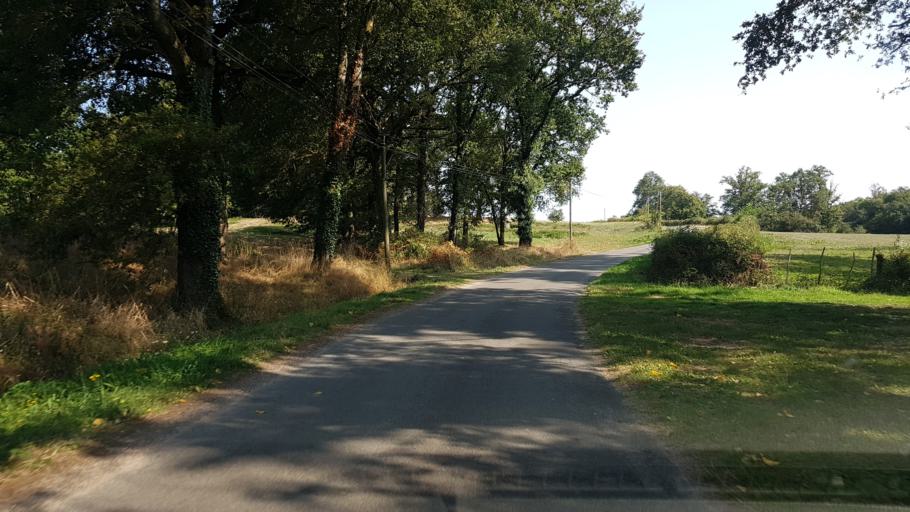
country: FR
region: Poitou-Charentes
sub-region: Departement de la Charente
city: Etagnac
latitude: 45.9005
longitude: 0.7742
